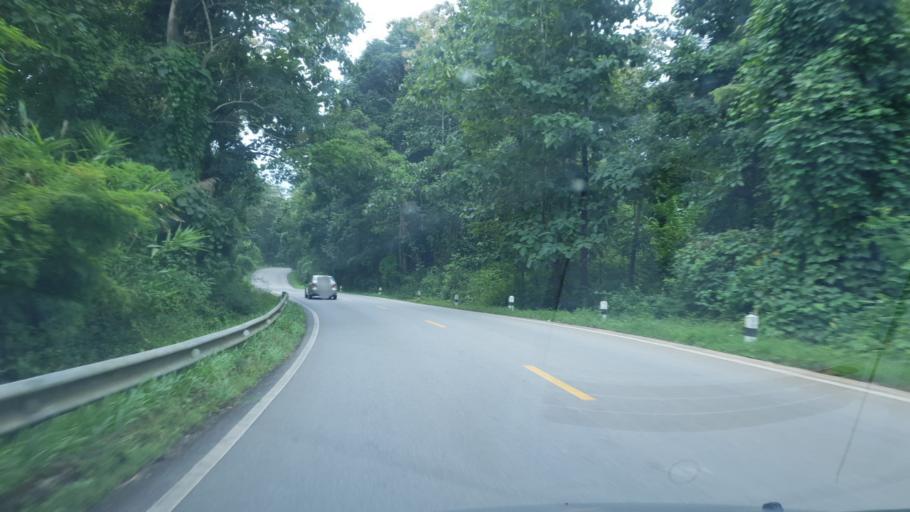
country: TH
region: Mae Hong Son
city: Khun Yuam
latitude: 18.7145
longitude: 97.9091
